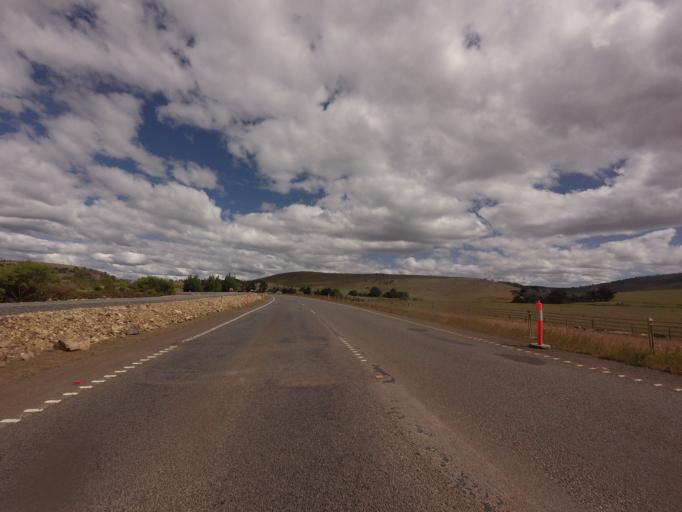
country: AU
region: Tasmania
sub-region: Brighton
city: Bridgewater
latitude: -42.1973
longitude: 147.3922
